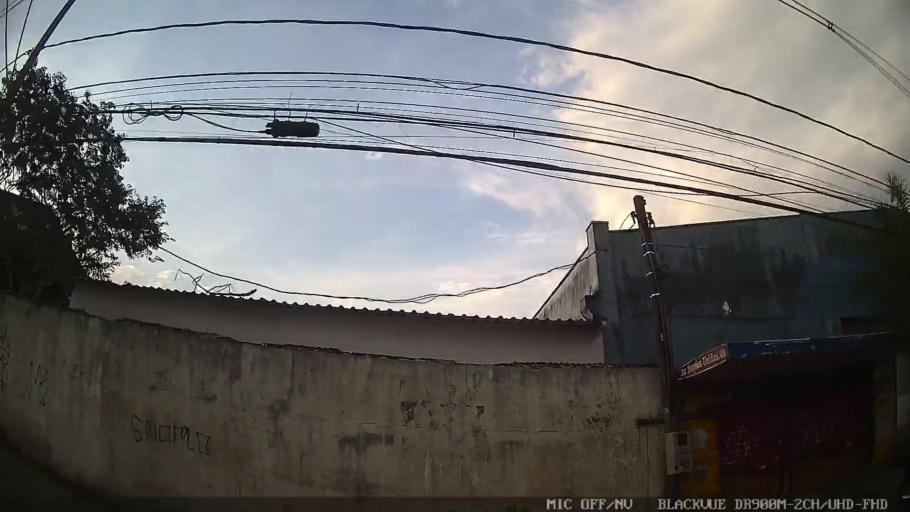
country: BR
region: Sao Paulo
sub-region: Cubatao
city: Cubatao
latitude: -23.8963
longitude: -46.4221
